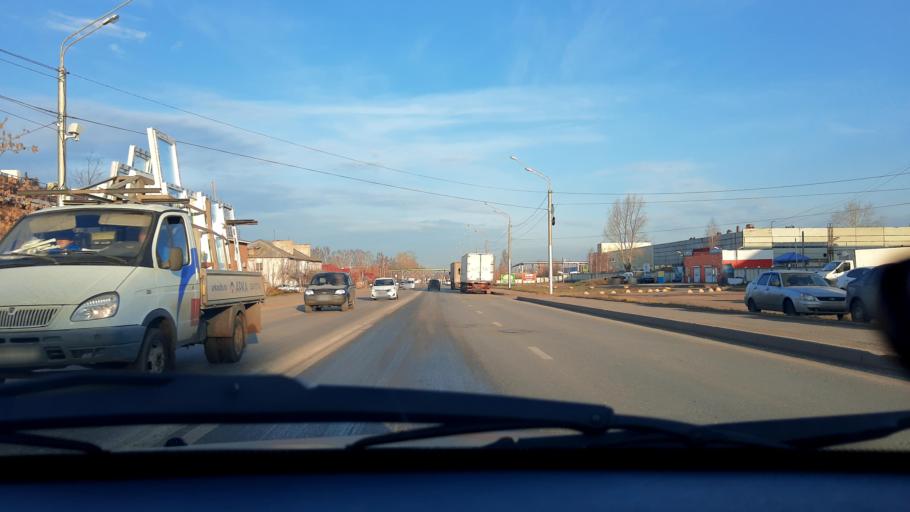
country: RU
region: Bashkortostan
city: Iglino
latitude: 54.7600
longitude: 56.2441
